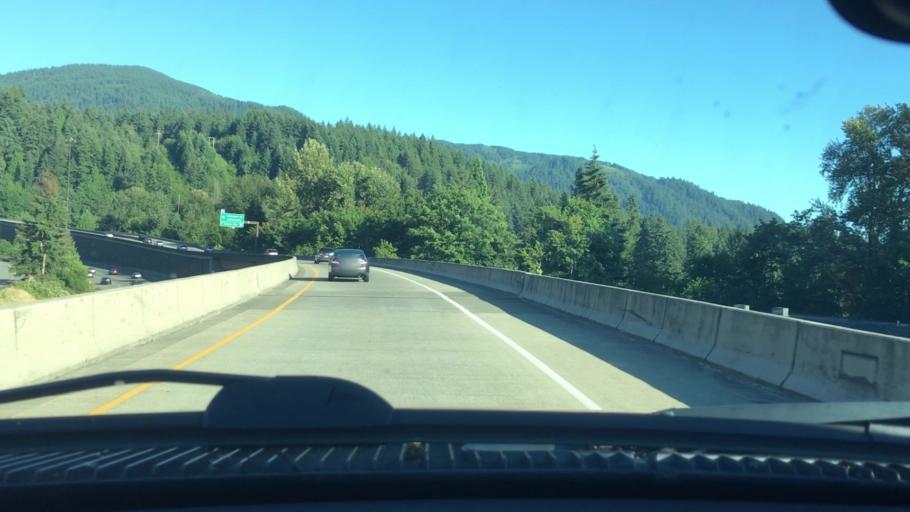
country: US
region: Washington
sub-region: King County
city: Issaquah
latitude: 47.5334
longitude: -122.0299
